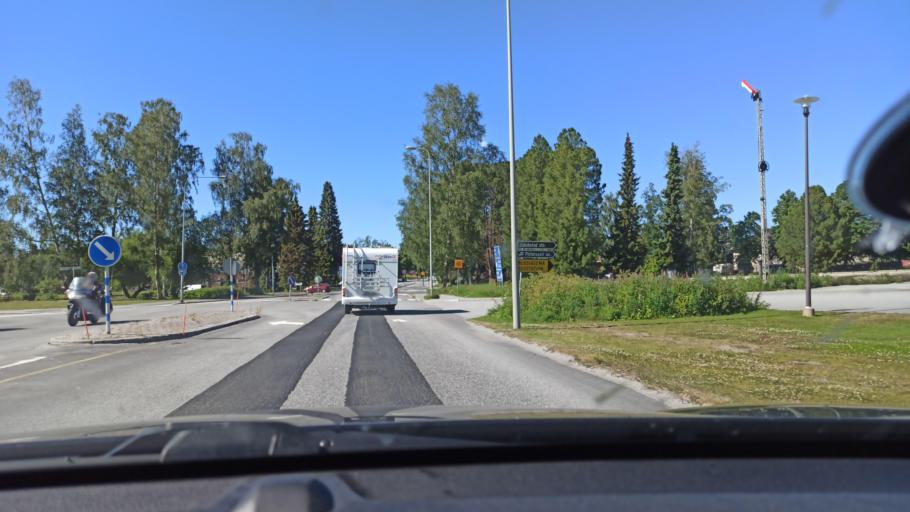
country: FI
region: Ostrobothnia
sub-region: Jakobstadsregionen
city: Jakobstad
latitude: 63.6740
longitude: 22.7132
